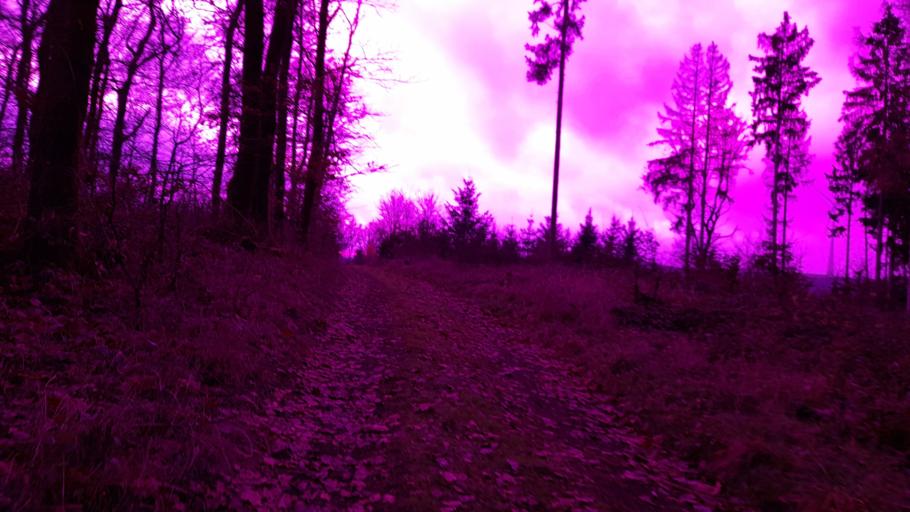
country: DE
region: Rheinland-Pfalz
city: Dasburg
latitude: 50.0653
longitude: 6.1077
